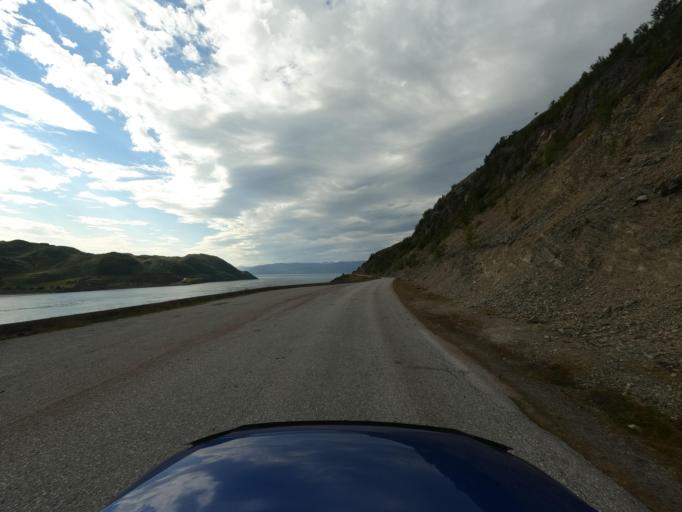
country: NO
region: Finnmark Fylke
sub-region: Kvalsund
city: Kvalsund
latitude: 70.5088
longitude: 23.9113
